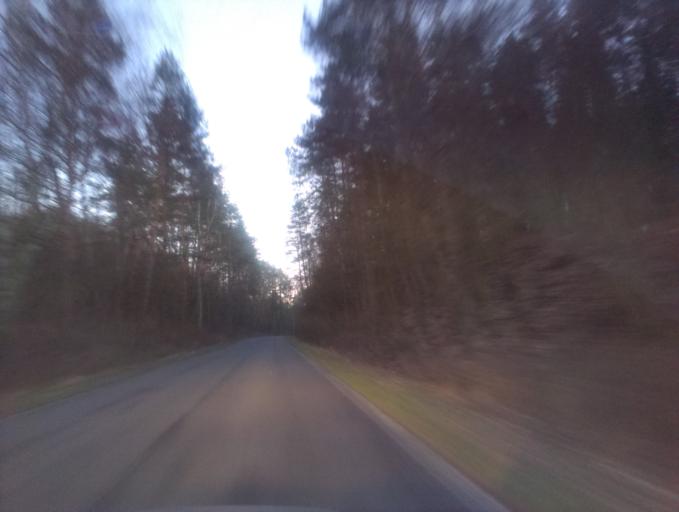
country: PL
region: Greater Poland Voivodeship
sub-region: Powiat zlotowski
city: Zlotow
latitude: 53.4892
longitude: 16.9891
